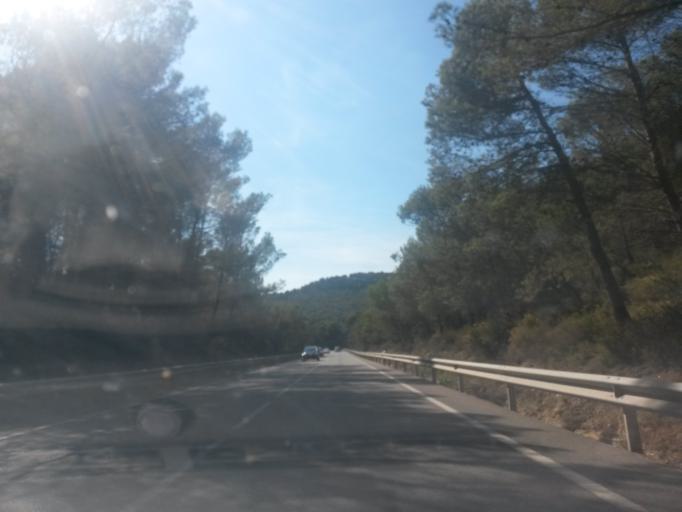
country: ES
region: Catalonia
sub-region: Provincia de Girona
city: Regencos
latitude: 41.9531
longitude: 3.1817
